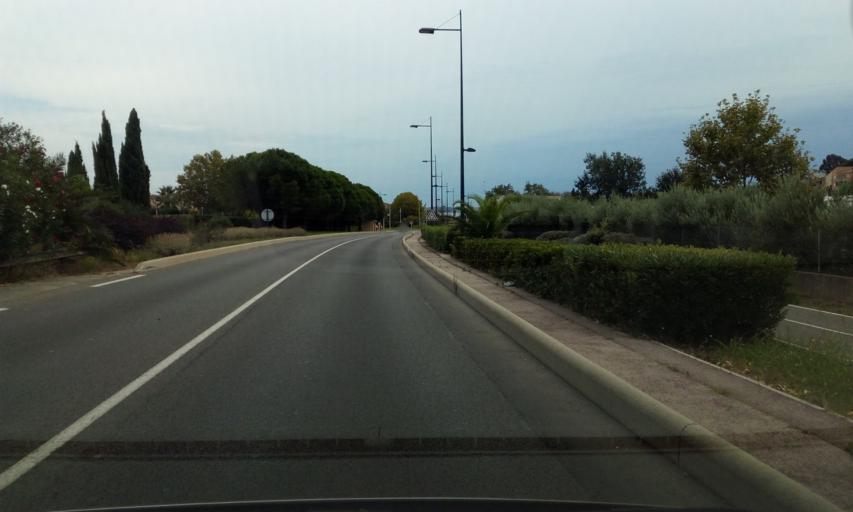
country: FR
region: Provence-Alpes-Cote d'Azur
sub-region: Departement du Var
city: Carqueiranne
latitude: 43.0974
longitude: 6.0677
